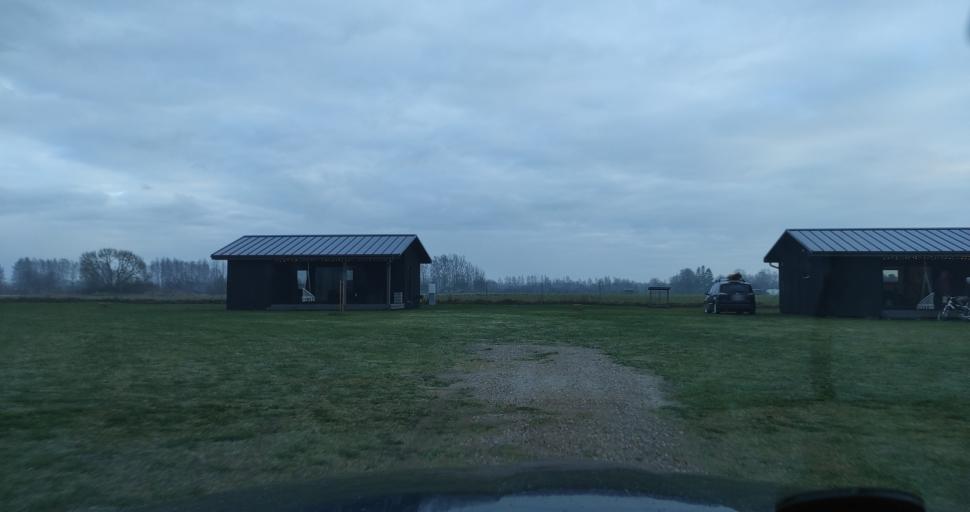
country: LV
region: Ventspils
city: Ventspils
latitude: 57.2379
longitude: 21.4367
